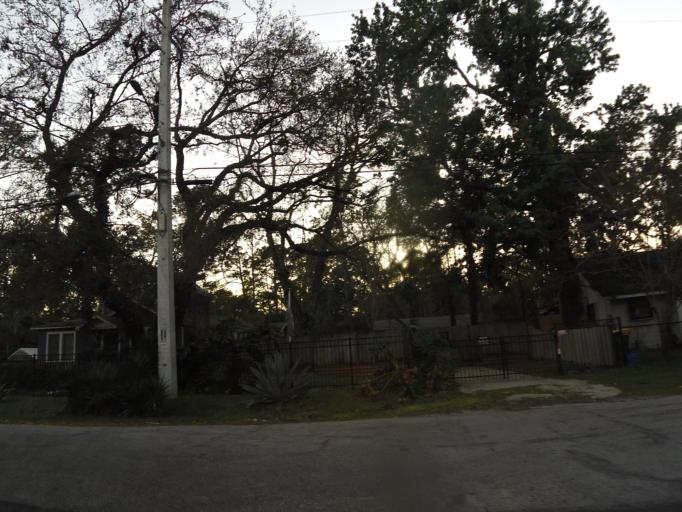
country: US
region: Florida
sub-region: Duval County
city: Jacksonville
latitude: 30.2775
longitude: -81.6310
